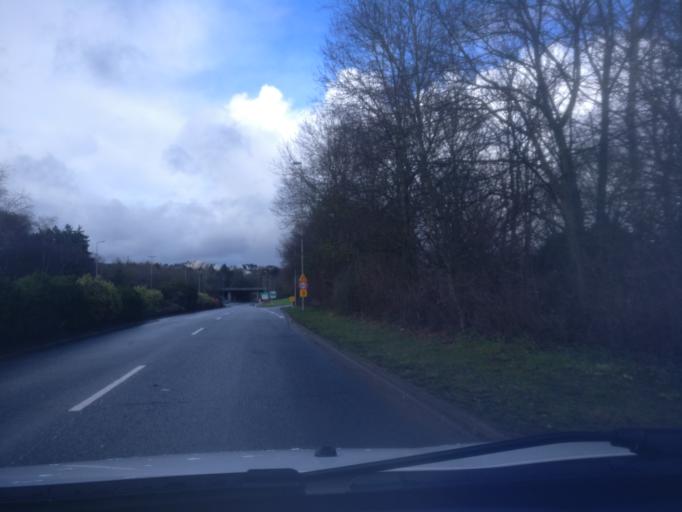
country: FR
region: Lower Normandy
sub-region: Departement du Calvados
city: Caen
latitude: 49.1947
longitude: -0.3747
